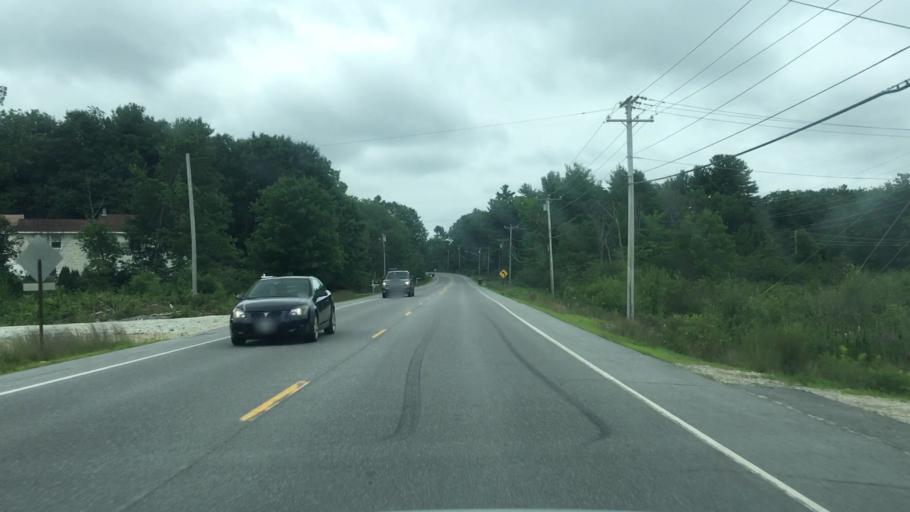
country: US
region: Maine
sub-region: York County
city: Biddeford
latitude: 43.5294
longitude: -70.5025
